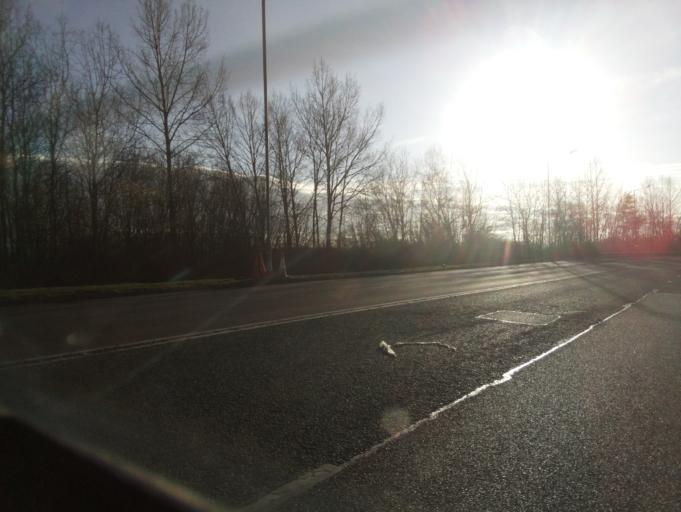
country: GB
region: England
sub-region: Derbyshire
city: Findern
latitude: 52.8702
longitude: -1.5640
